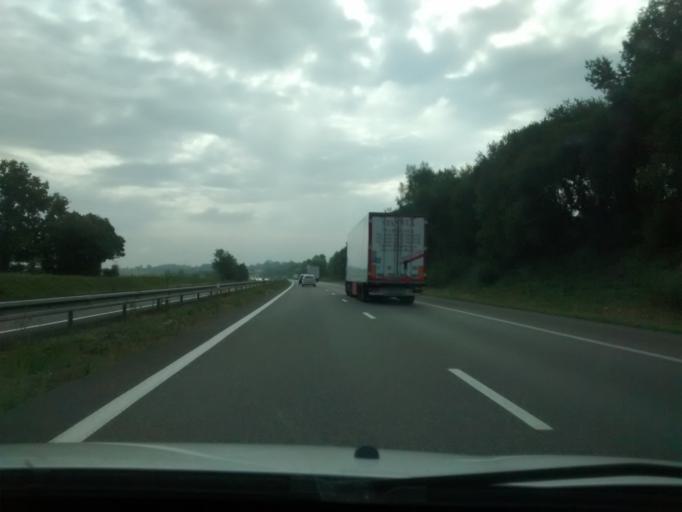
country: FR
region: Pays de la Loire
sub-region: Departement de la Mayenne
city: Loiron
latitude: 48.0751
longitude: -0.9500
